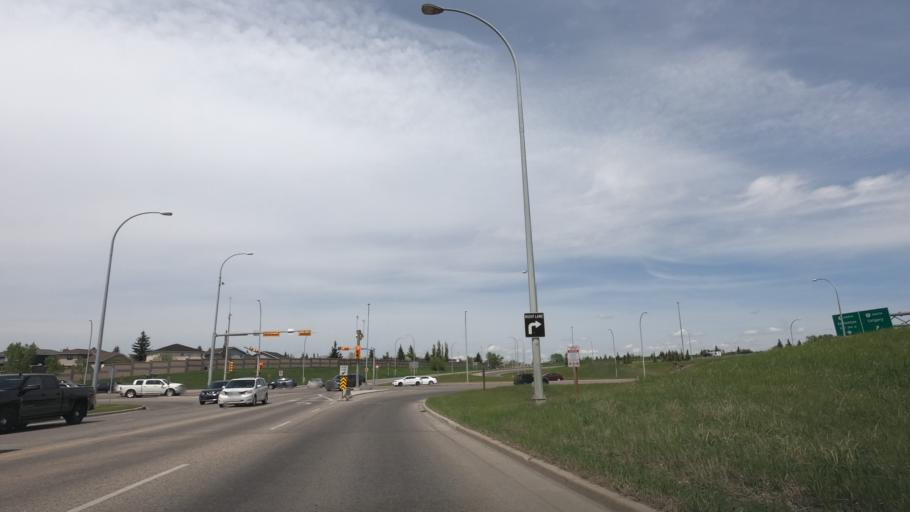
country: CA
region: Alberta
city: Airdrie
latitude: 51.2697
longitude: -114.0036
